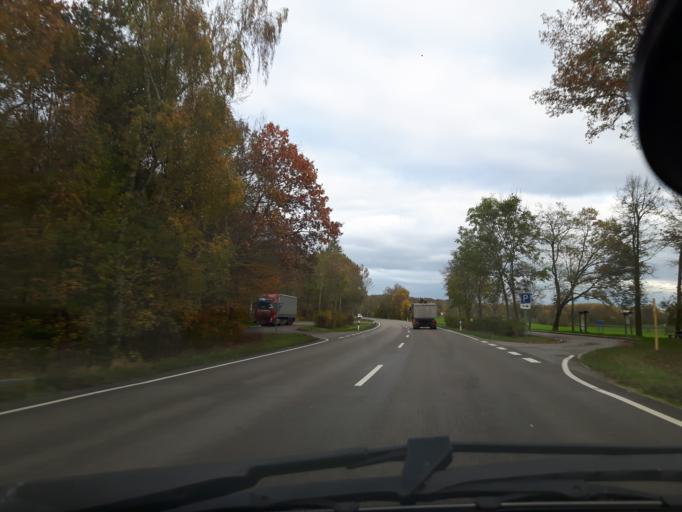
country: DE
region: Bavaria
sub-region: Regierungsbezirk Mittelfranken
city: Weidenbach
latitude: 49.2117
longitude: 10.6487
